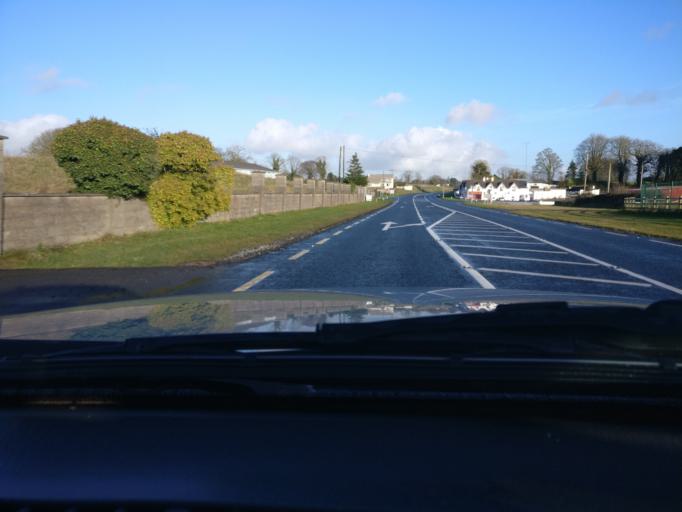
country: IE
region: Leinster
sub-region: An Iarmhi
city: An Muileann gCearr
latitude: 53.5526
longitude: -7.2452
